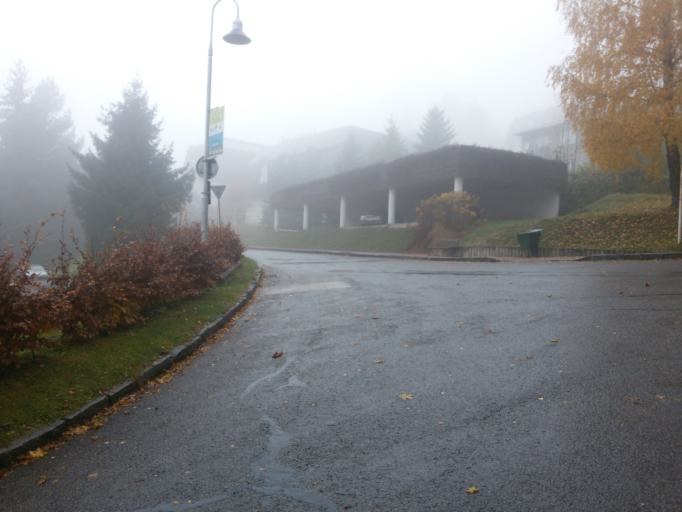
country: CZ
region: Kralovehradecky
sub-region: Okres Trutnov
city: Svoboda nad Upou
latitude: 50.6322
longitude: 15.7844
